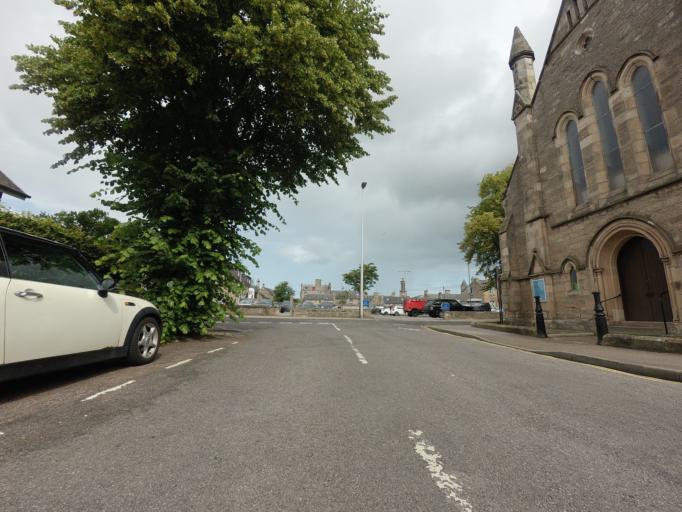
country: GB
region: Scotland
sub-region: Moray
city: Elgin
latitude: 57.6465
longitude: -3.3141
